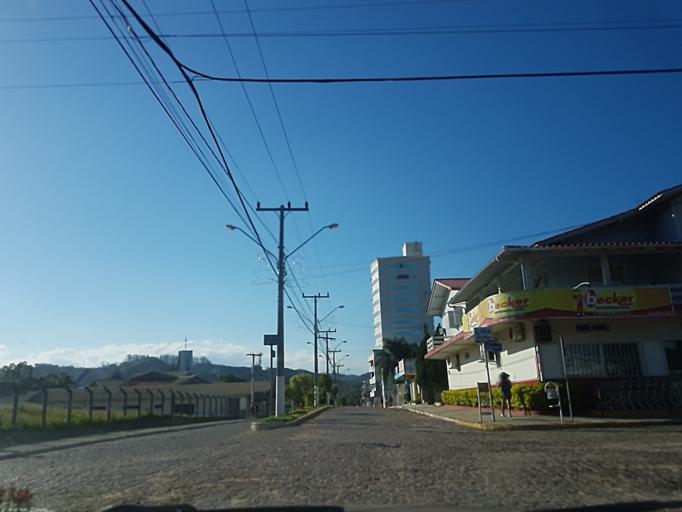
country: BR
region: Santa Catarina
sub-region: Braco Do Norte
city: Braco do Norte
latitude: -28.3274
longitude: -49.1739
